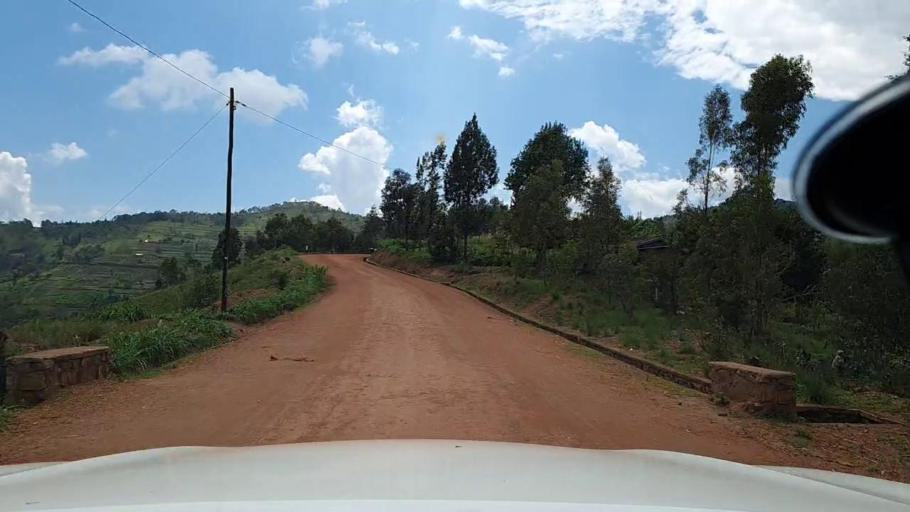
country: RW
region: Kigali
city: Kigali
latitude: -1.7736
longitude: 29.8421
